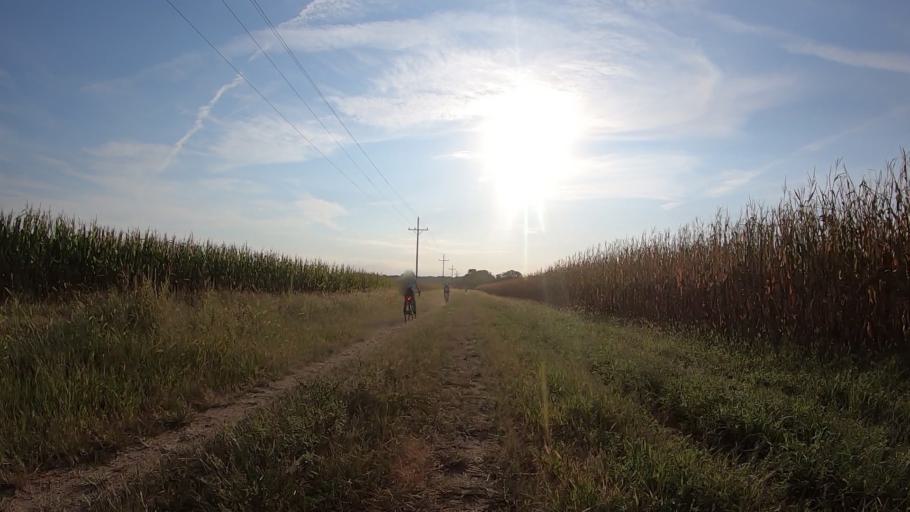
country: US
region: Kansas
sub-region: Marshall County
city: Blue Rapids
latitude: 39.7118
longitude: -96.7859
